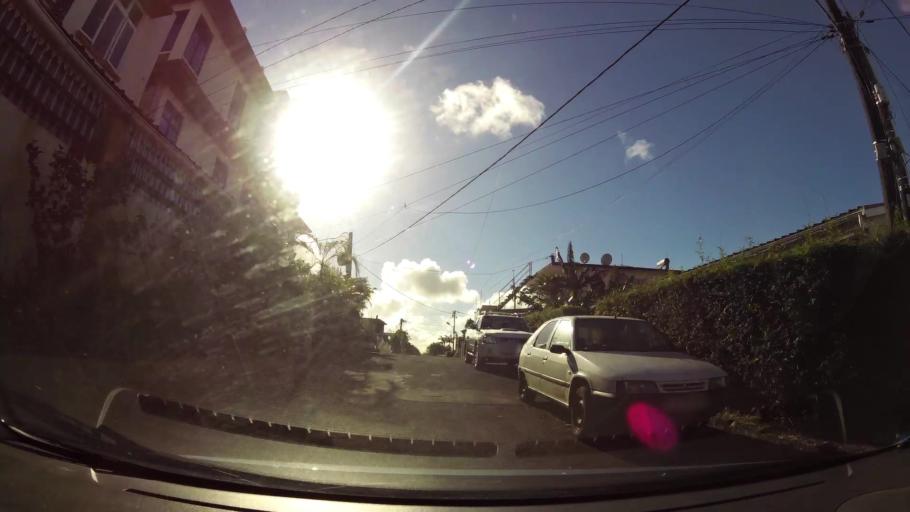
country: MU
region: Plaines Wilhems
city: Curepipe
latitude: -20.3181
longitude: 57.5369
